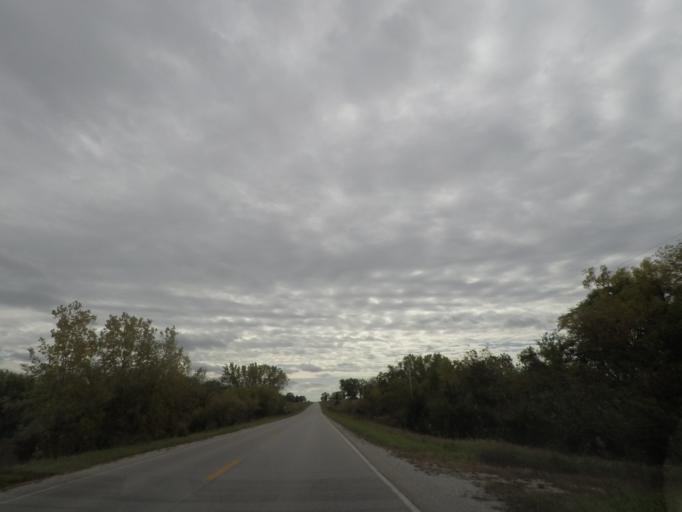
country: US
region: Iowa
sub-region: Story County
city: Huxley
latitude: 41.8687
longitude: -93.5316
